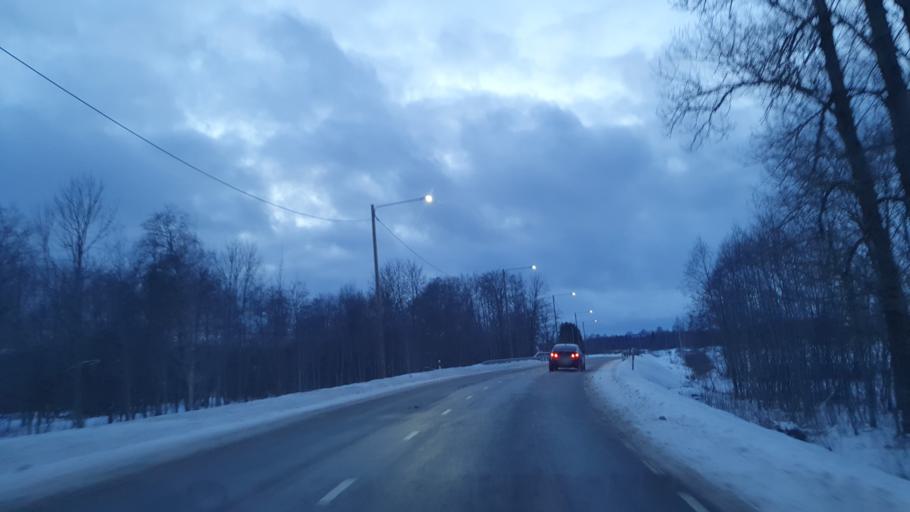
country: EE
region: Jogevamaa
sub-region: Jogeva linn
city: Jogeva
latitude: 58.5793
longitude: 26.3010
